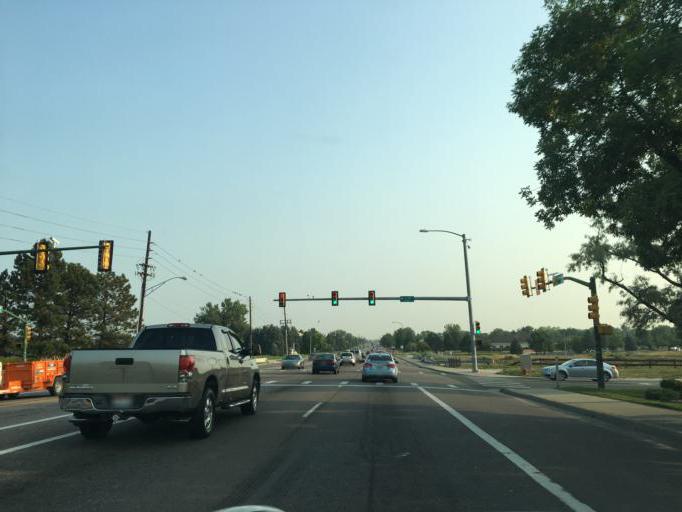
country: US
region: Colorado
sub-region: Adams County
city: Westminster
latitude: 39.8341
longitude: -105.0532
